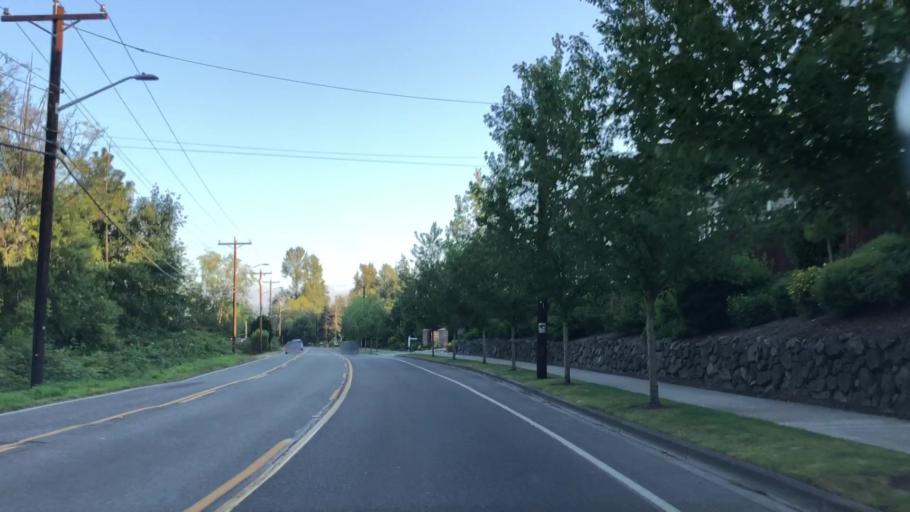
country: US
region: Washington
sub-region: Snohomish County
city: Martha Lake
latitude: 47.8566
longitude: -122.2717
